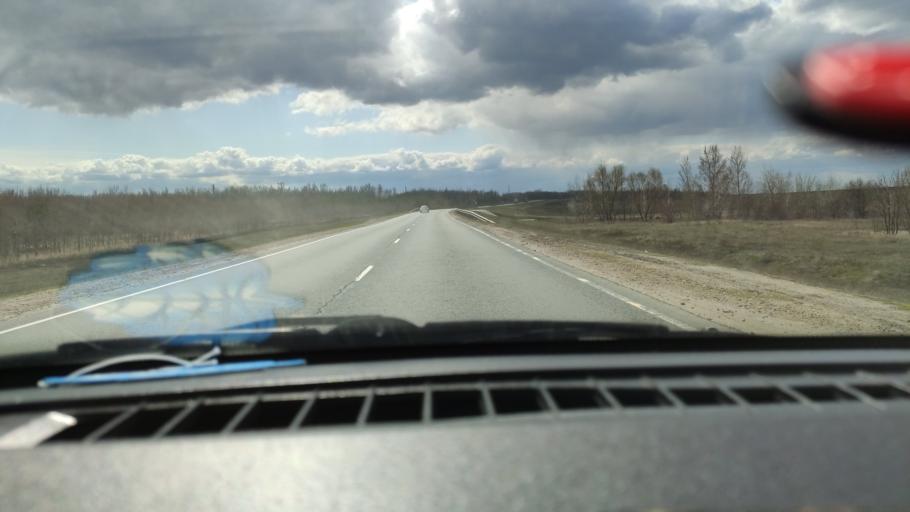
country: RU
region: Saratov
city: Alekseyevka
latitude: 52.2764
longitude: 47.9312
